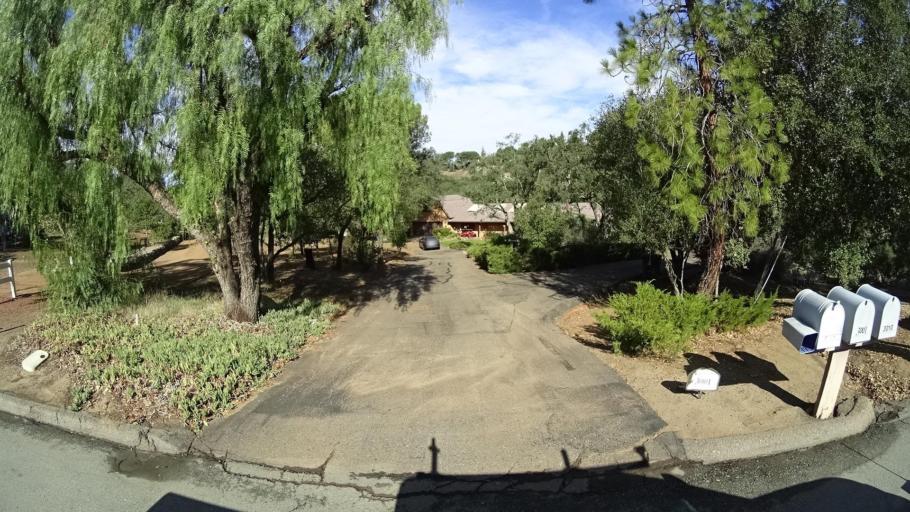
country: US
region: California
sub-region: San Diego County
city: Alpine
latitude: 32.8219
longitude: -116.7486
